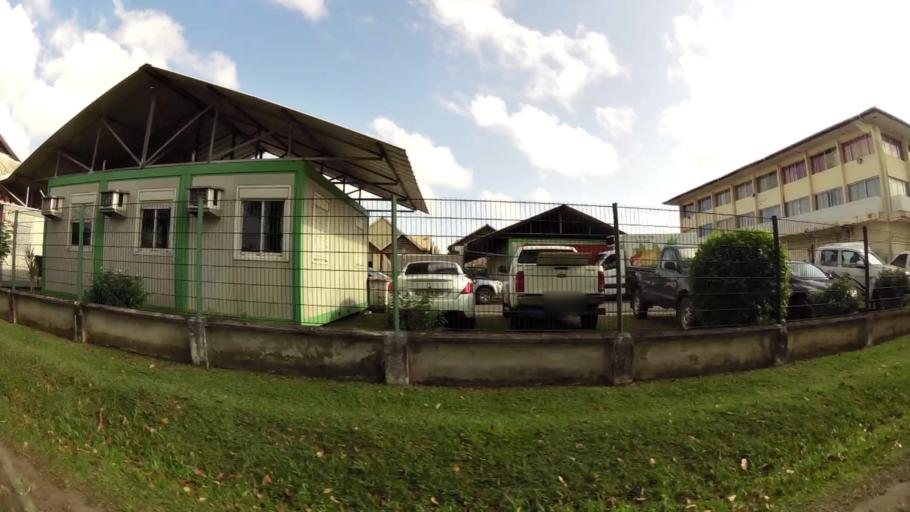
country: GF
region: Guyane
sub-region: Guyane
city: Cayenne
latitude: 4.9383
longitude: -52.3222
